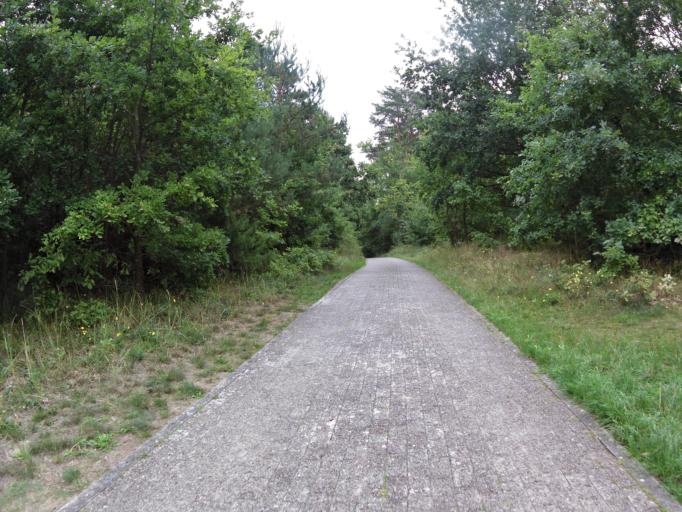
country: PL
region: West Pomeranian Voivodeship
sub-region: Swinoujscie
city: Swinoujscie
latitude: 53.8751
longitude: 14.1821
